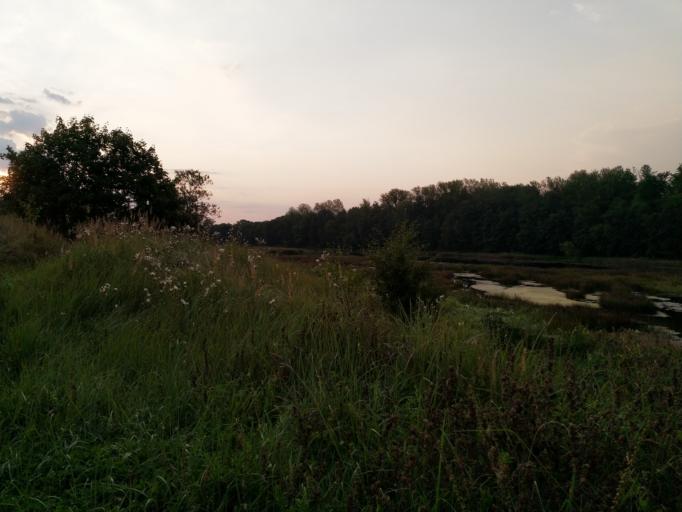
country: LV
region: Kuldigas Rajons
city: Kuldiga
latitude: 56.9681
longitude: 21.9819
